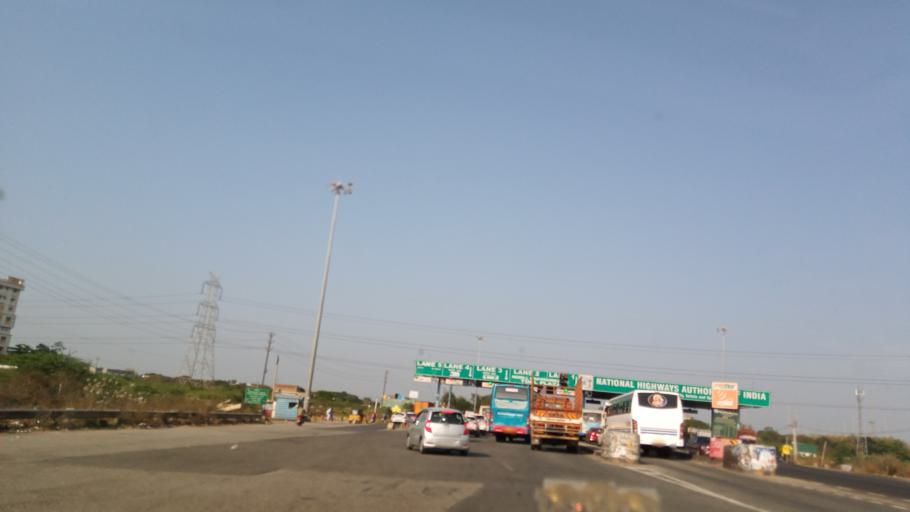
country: IN
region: Tamil Nadu
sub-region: Kancheepuram
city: Sriperumbudur
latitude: 12.9816
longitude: 79.9680
